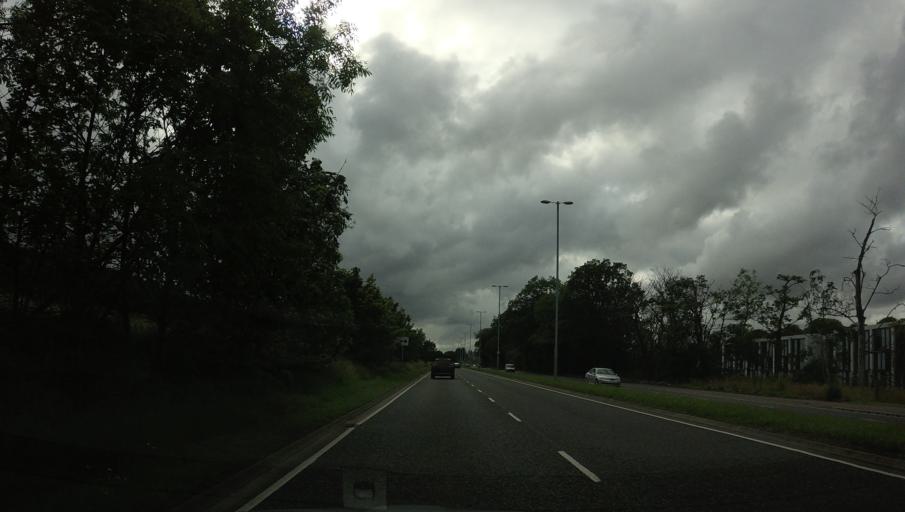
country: GB
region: Scotland
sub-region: Aberdeenshire
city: Westhill
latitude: 57.1465
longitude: -2.2268
